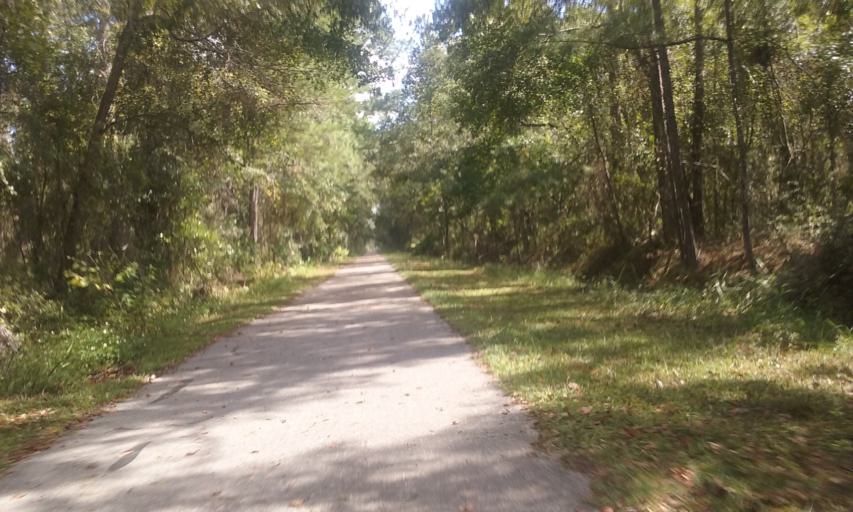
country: US
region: Florida
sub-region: Alachua County
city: Hawthorne
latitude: 29.5877
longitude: -82.1196
